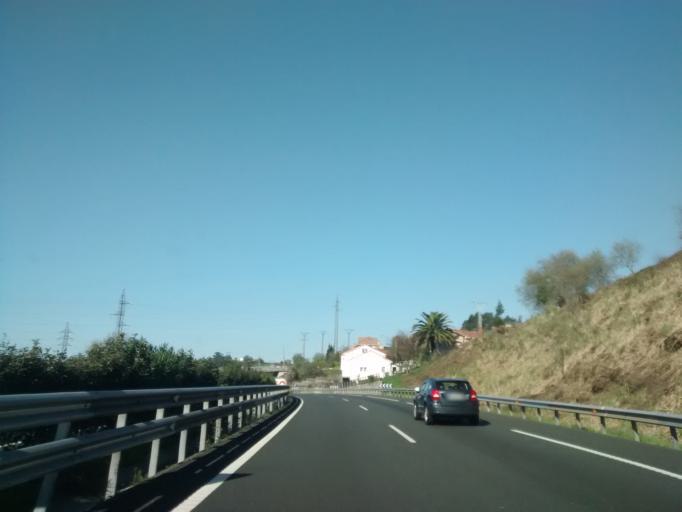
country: ES
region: Cantabria
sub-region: Provincia de Cantabria
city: Torrelavega
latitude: 43.3694
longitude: -4.0396
